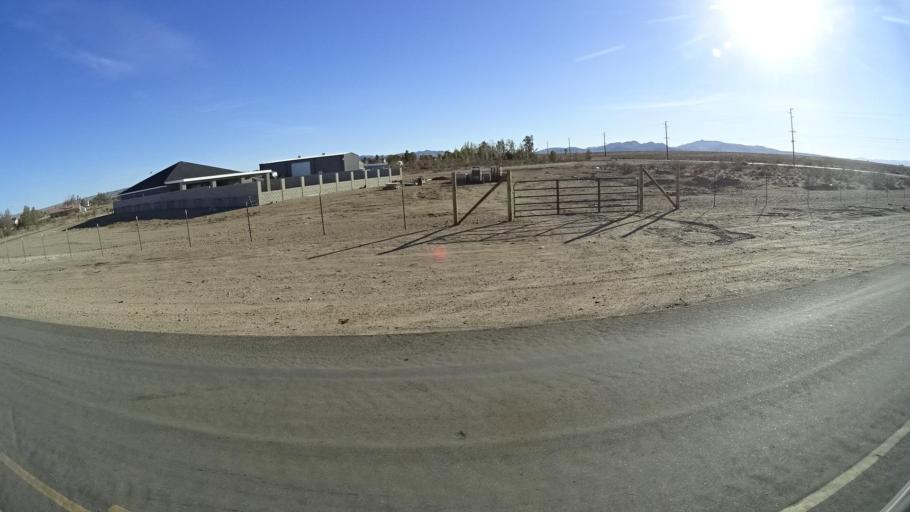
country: US
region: California
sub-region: Kern County
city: China Lake Acres
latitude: 35.6302
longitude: -117.7222
